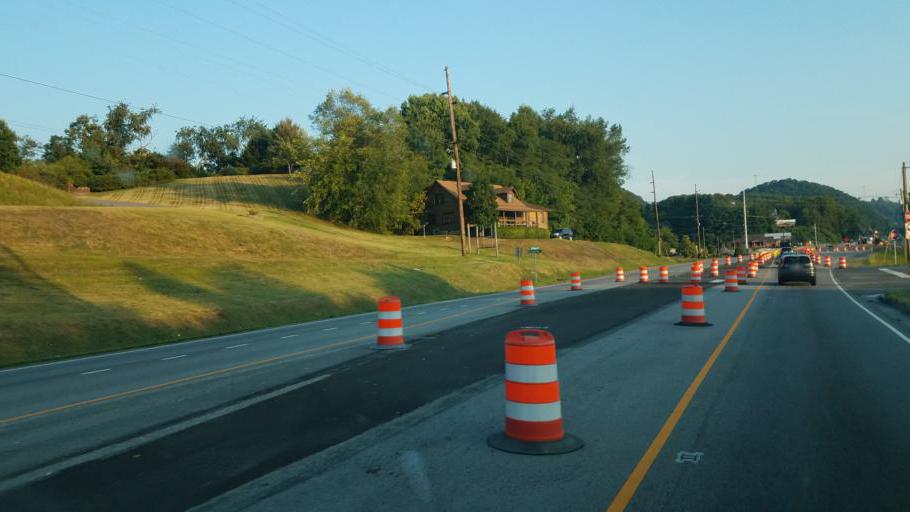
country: US
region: Virginia
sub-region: Scott County
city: Weber City
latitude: 36.6111
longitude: -82.5684
